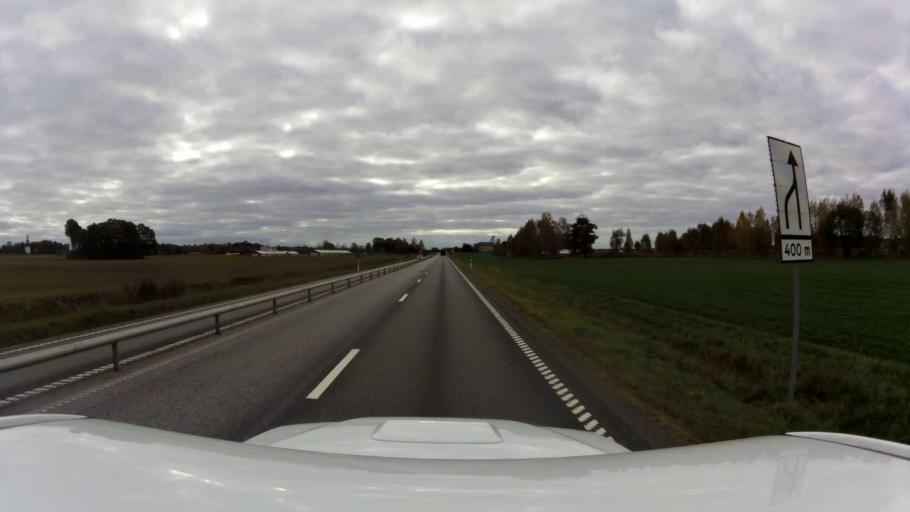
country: SE
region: OEstergoetland
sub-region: Linkopings Kommun
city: Malmslatt
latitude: 58.3482
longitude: 15.5503
